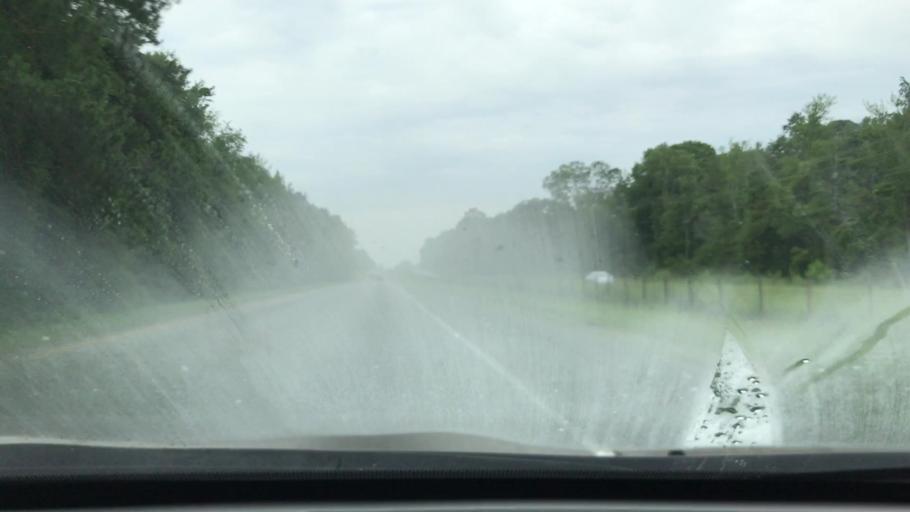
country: US
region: South Carolina
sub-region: Jasper County
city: Ridgeland
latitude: 32.5350
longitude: -80.9563
